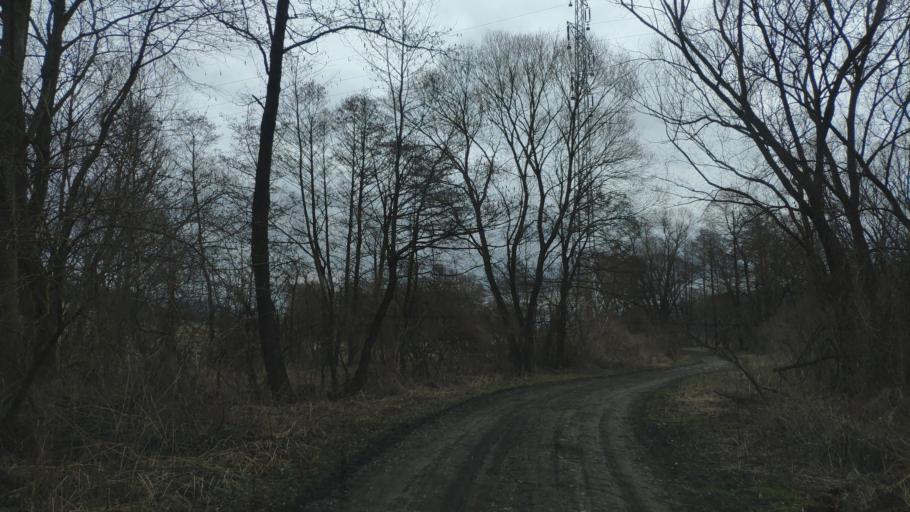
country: SK
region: Presovsky
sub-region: Okres Presov
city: Presov
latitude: 49.0761
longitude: 21.2945
